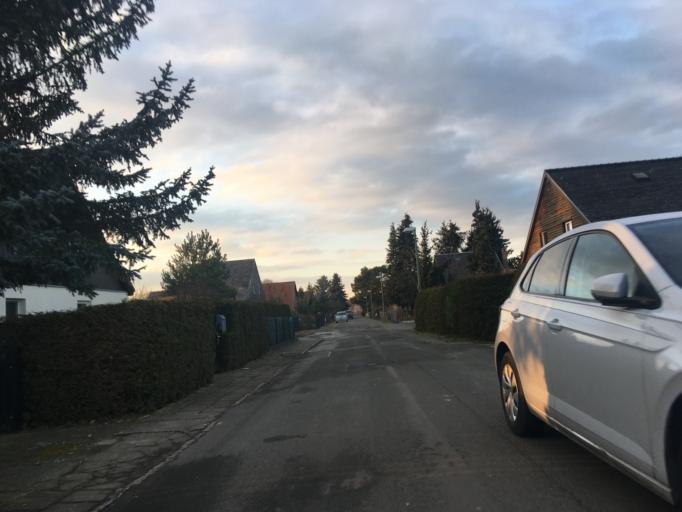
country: DE
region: Berlin
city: Buch
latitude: 52.6187
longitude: 13.4944
